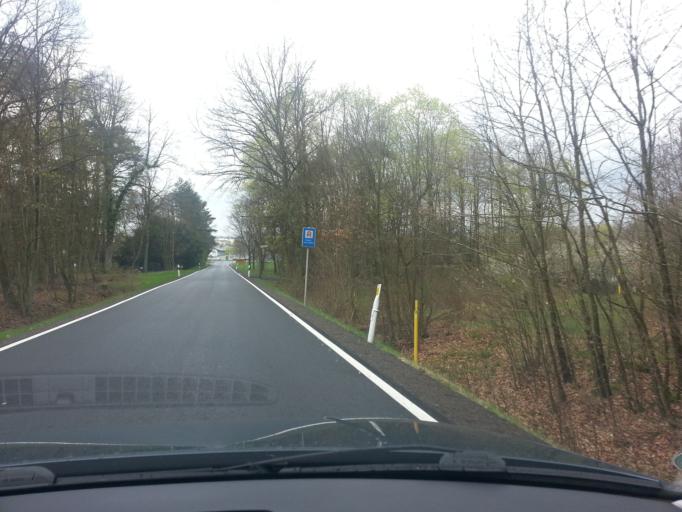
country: DE
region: Saarland
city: Homburg
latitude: 49.3277
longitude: 7.3610
